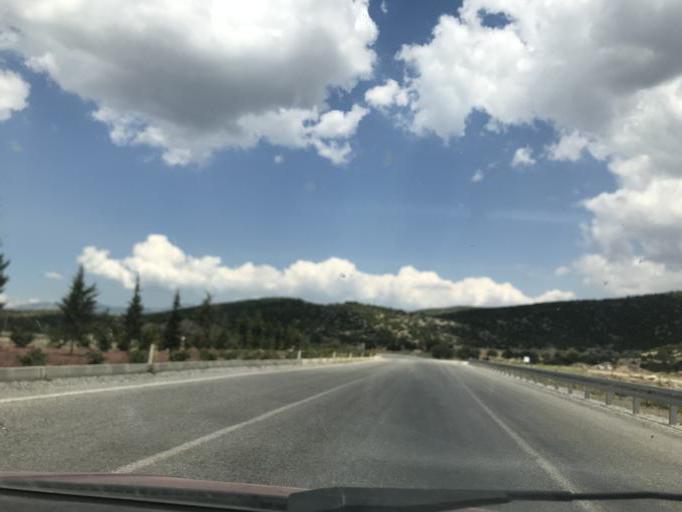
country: TR
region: Denizli
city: Tavas
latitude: 37.5821
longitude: 29.0969
